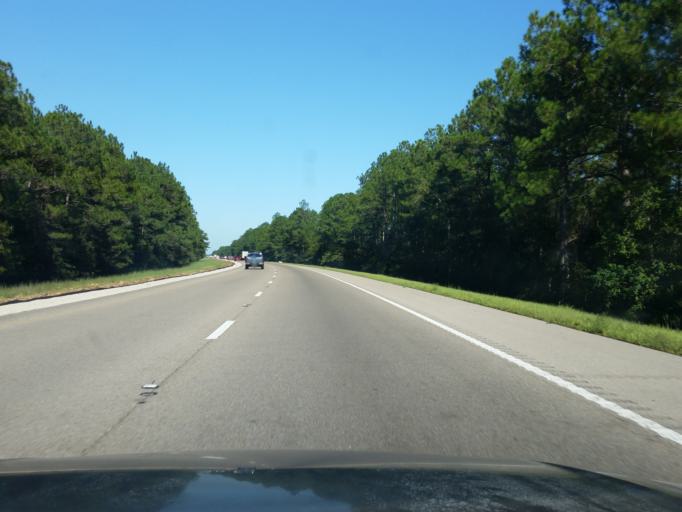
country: US
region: Mississippi
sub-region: Hancock County
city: Kiln
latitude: 30.3310
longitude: -89.5238
